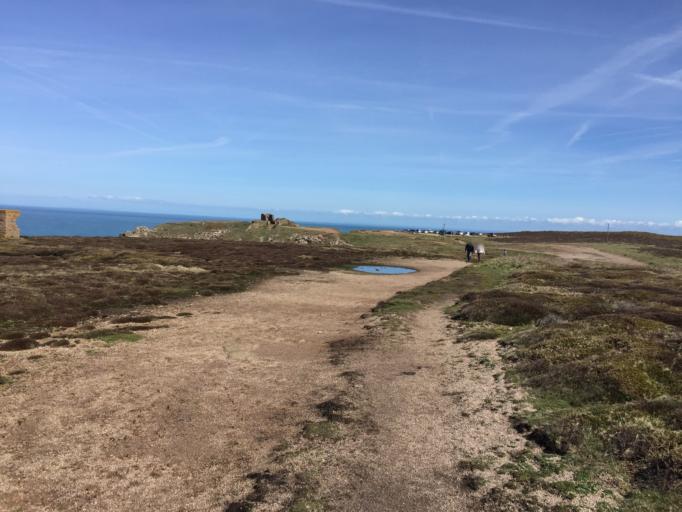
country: JE
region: St Helier
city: Saint Helier
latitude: 49.2548
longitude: -2.2478
